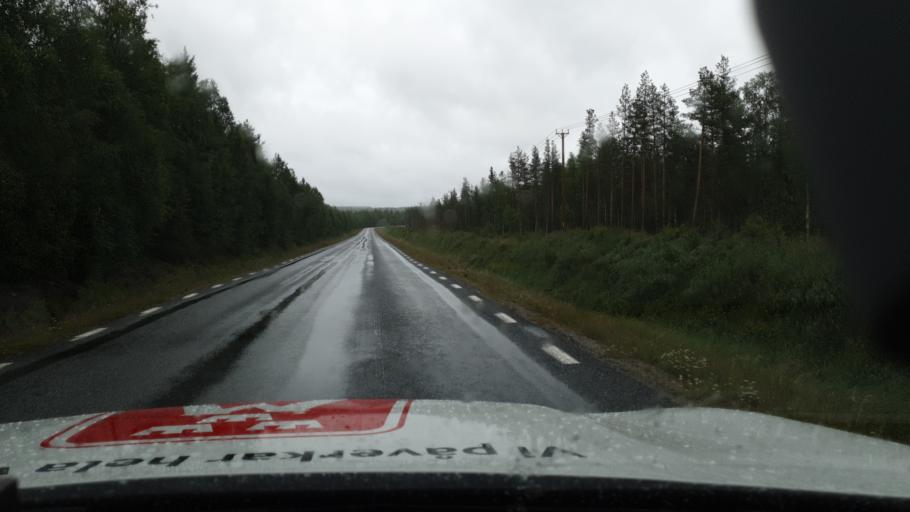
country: SE
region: Vaesterbotten
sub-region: Asele Kommun
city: Insjon
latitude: 64.2720
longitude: 17.5803
